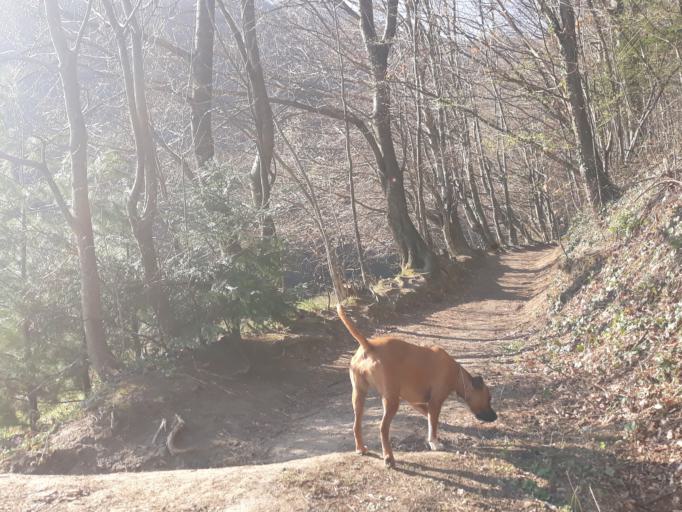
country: HR
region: Varazdinska
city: Ivanec
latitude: 46.1952
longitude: 16.1377
